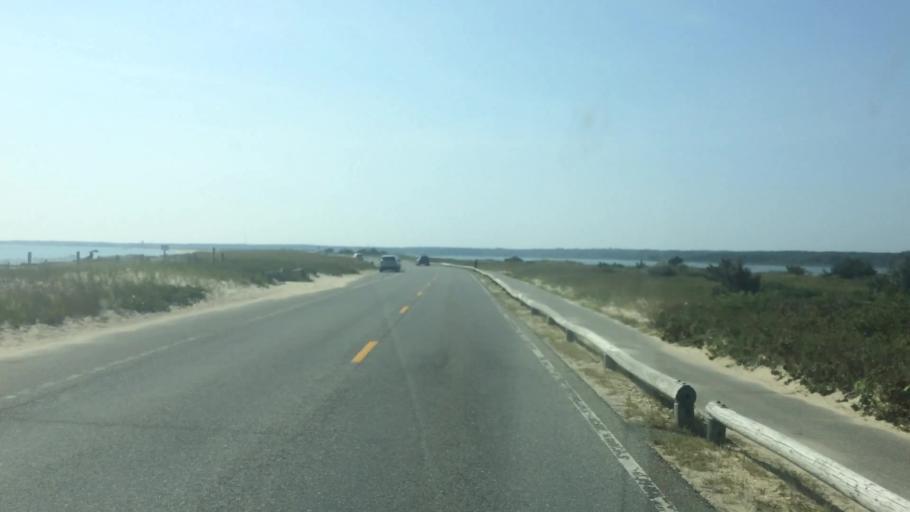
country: US
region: Massachusetts
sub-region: Dukes County
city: Oak Bluffs
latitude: 41.4287
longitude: -70.5557
